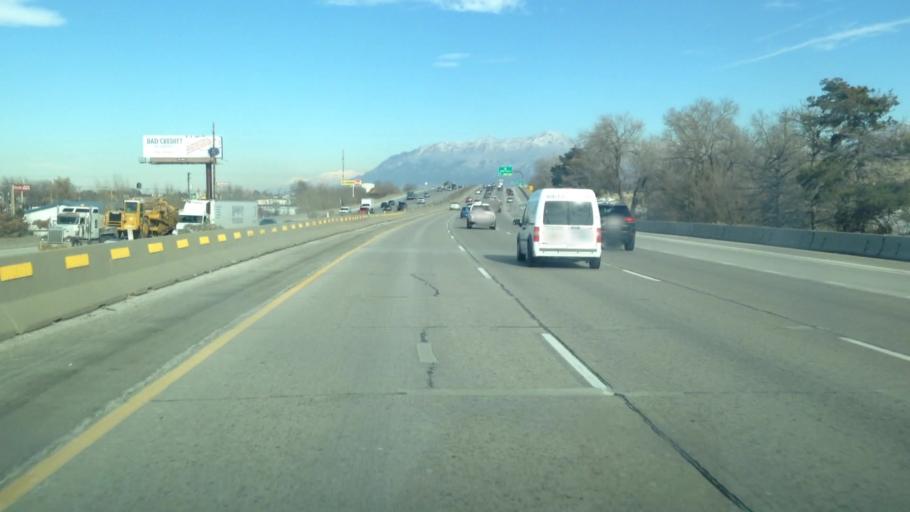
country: US
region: Utah
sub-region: Weber County
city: Roy
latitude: 41.1528
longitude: -112.0252
